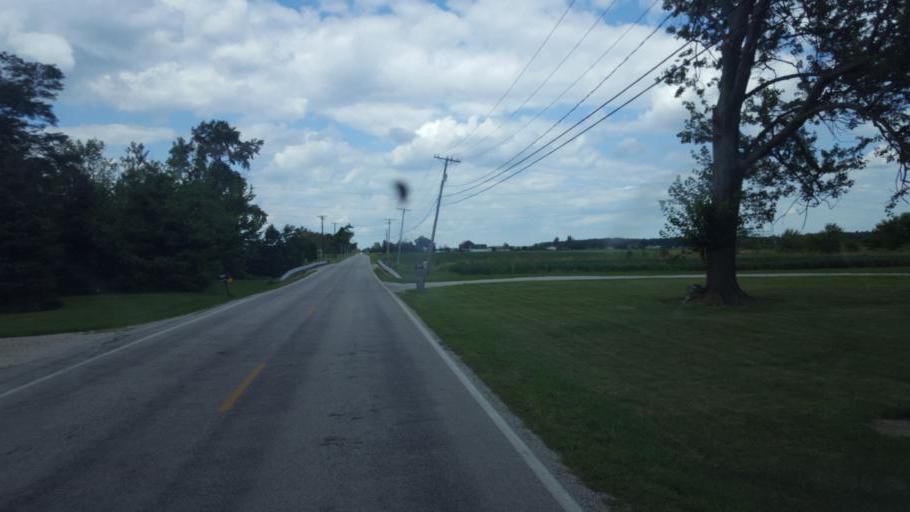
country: US
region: Ohio
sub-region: Ottawa County
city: Elmore
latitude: 41.5521
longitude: -83.2803
